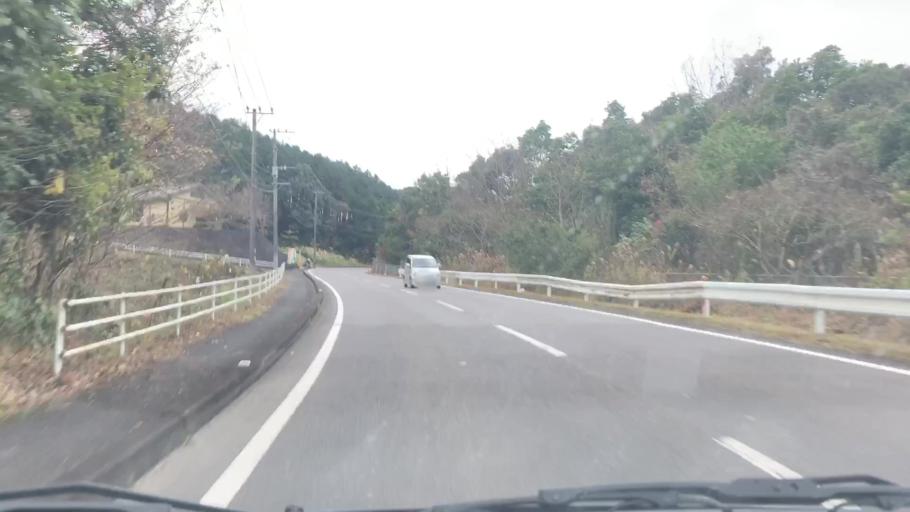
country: JP
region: Saga Prefecture
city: Ureshinomachi-shimojuku
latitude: 33.1129
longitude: 129.9761
